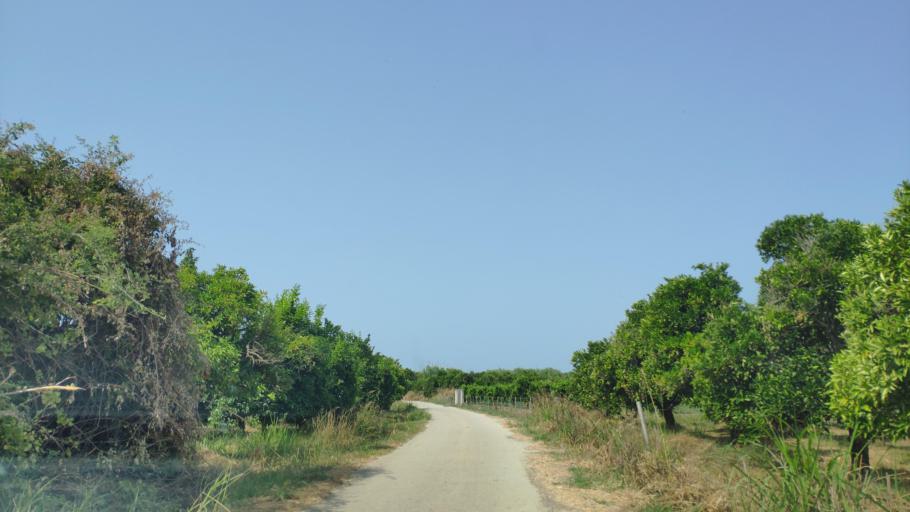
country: GR
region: Epirus
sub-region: Nomos Artas
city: Kompoti
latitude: 39.0626
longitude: 21.0754
